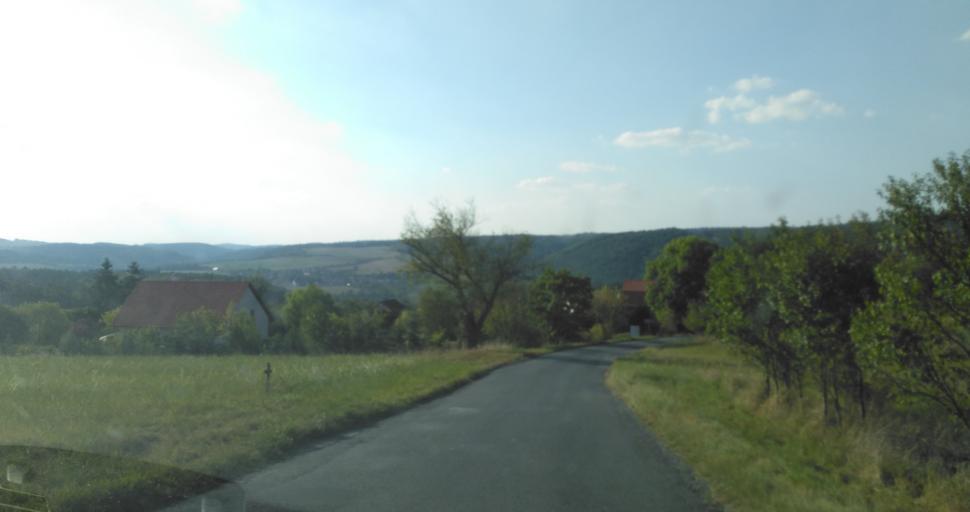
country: CZ
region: Central Bohemia
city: Roztoky
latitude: 50.0075
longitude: 13.8475
